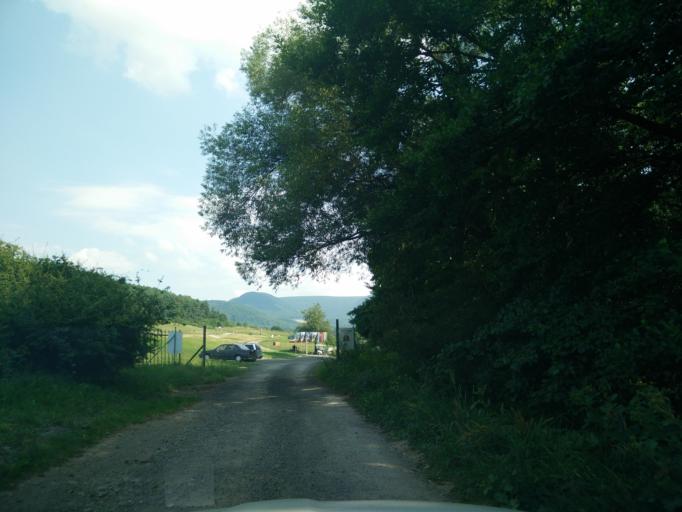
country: SK
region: Nitriansky
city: Prievidza
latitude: 48.7241
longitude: 18.6329
